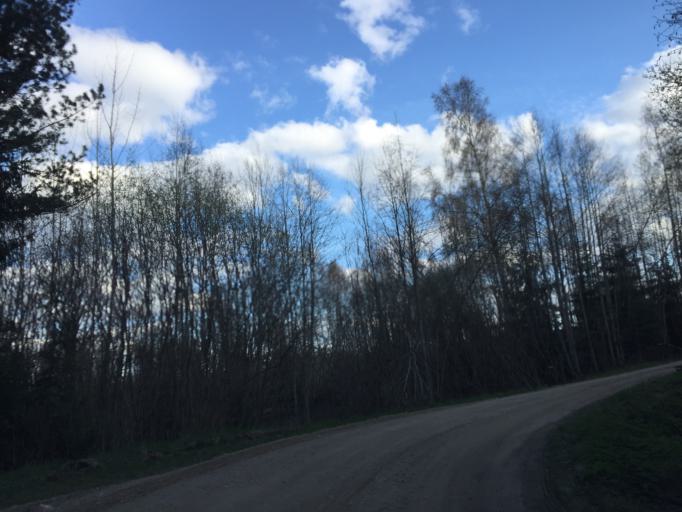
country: LV
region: Karsava
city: Karsava
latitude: 56.6802
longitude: 27.5231
